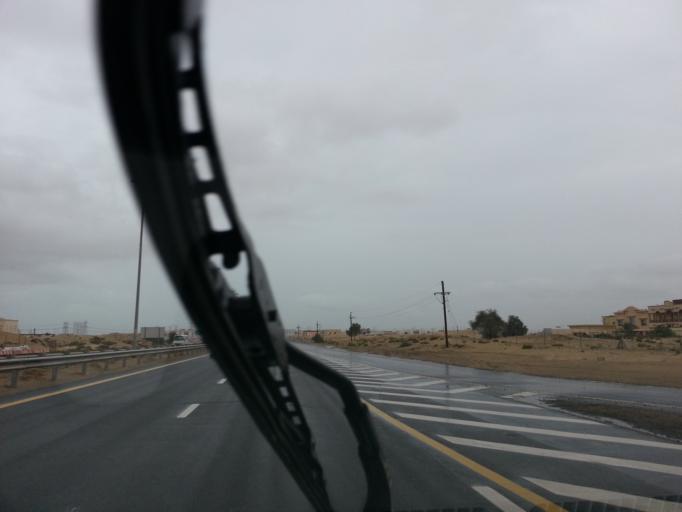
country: AE
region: Dubai
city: Dubai
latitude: 25.0628
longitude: 55.2208
